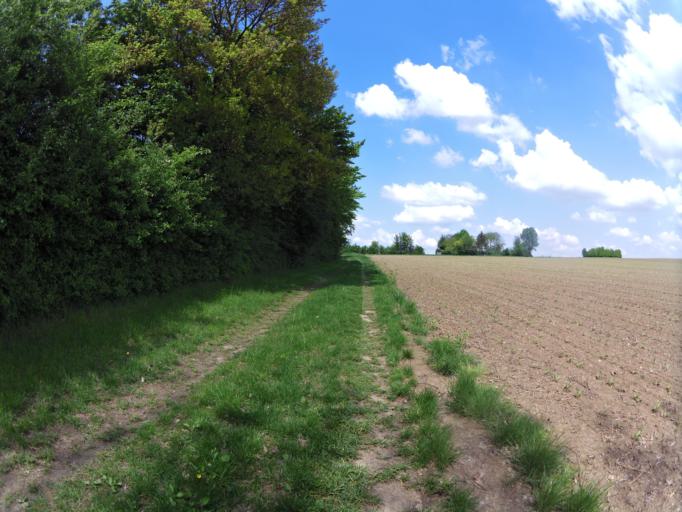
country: DE
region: Bavaria
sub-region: Regierungsbezirk Unterfranken
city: Sulzdorf
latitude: 49.6311
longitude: 9.9072
